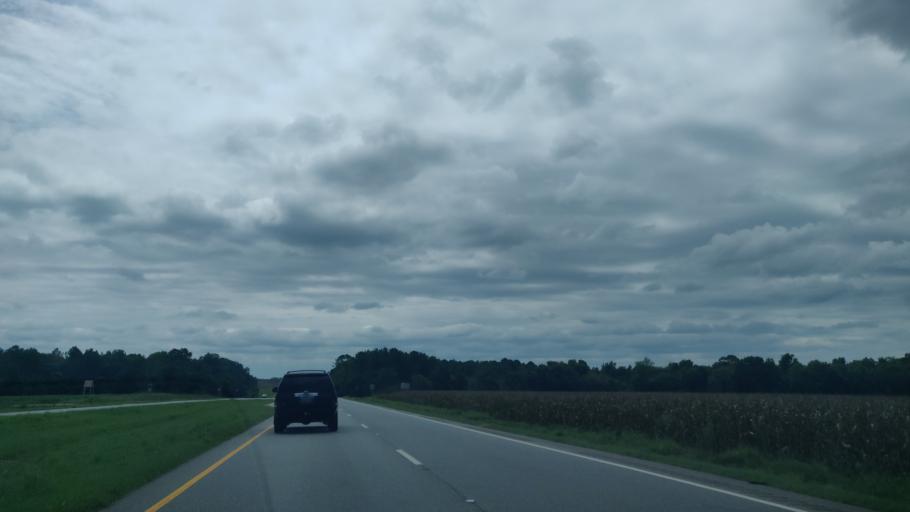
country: US
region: Georgia
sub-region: Terrell County
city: Dawson
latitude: 31.8559
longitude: -84.4792
